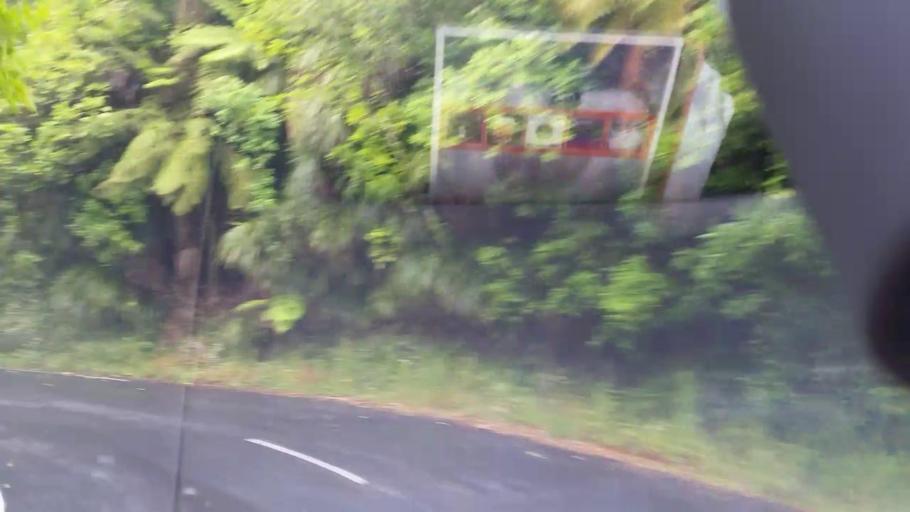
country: NZ
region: Auckland
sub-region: Auckland
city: Waitakere
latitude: -36.9100
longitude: 174.5690
